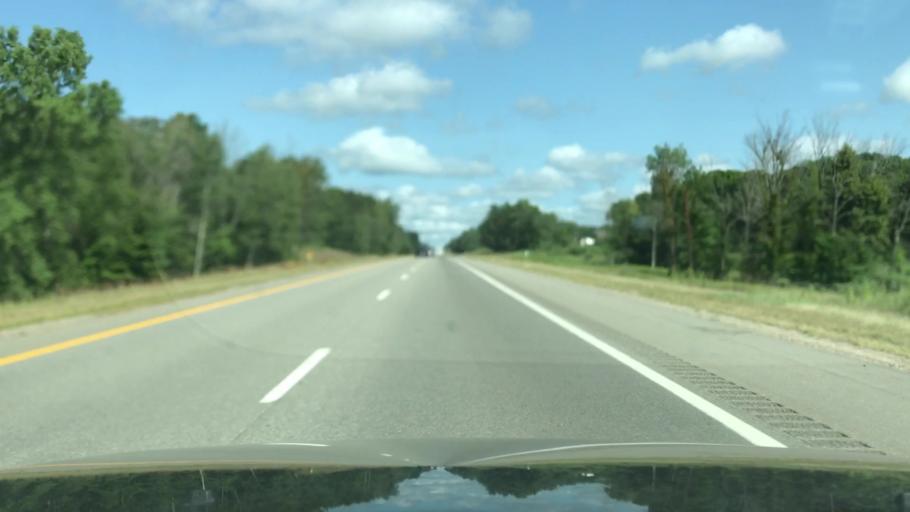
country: US
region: Michigan
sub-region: Mecosta County
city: Big Rapids
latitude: 43.6281
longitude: -85.5020
